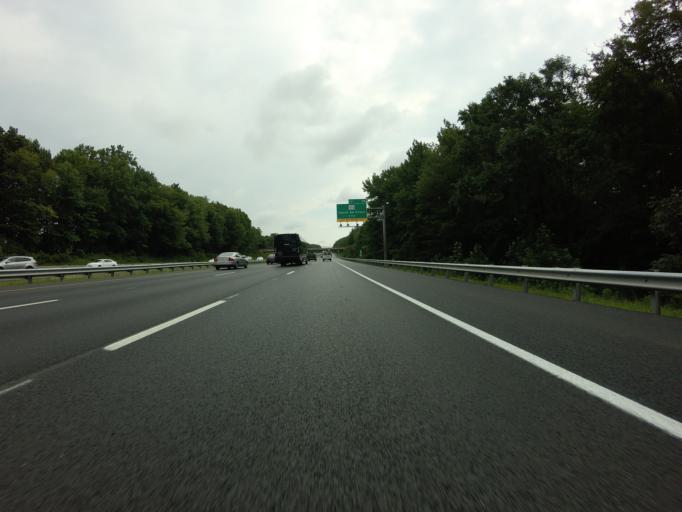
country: US
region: Maryland
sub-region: Harford County
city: Aberdeen
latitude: 39.5548
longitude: -76.1566
